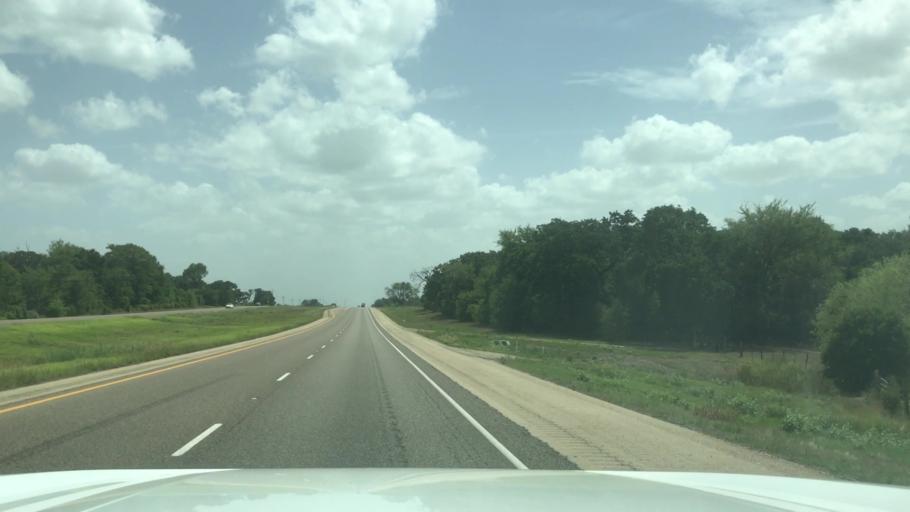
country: US
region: Texas
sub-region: Robertson County
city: Calvert
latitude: 31.0654
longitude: -96.7124
